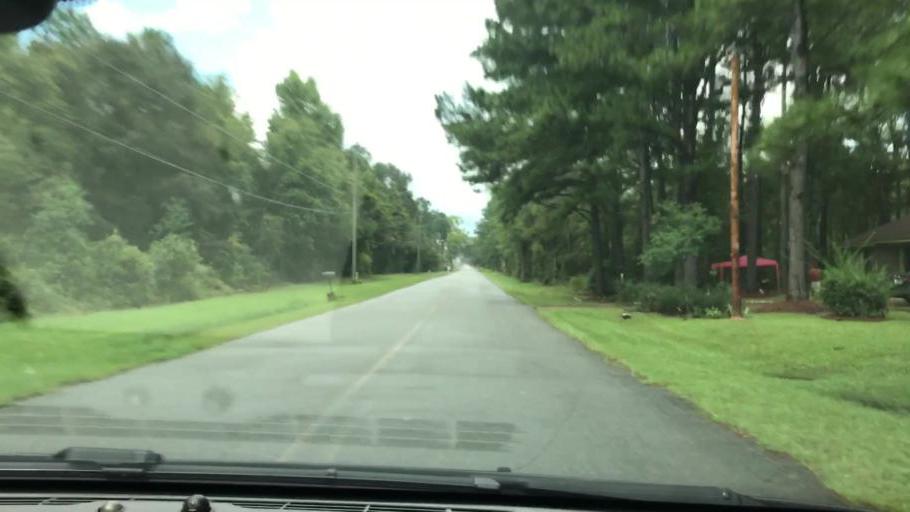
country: US
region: Georgia
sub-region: Early County
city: Blakely
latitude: 31.3665
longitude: -84.9473
